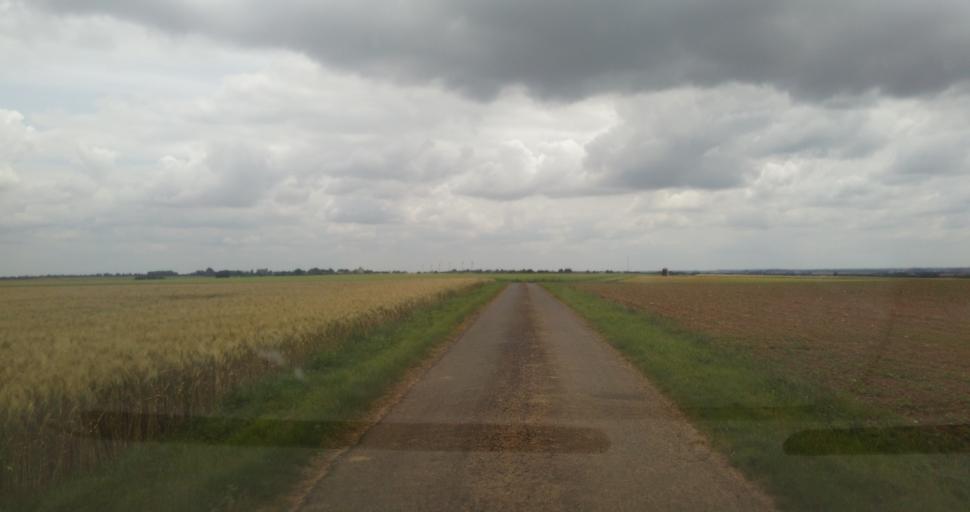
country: FR
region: Pays de la Loire
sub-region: Departement de la Vendee
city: Sainte-Gemme-la-Plaine
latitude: 46.5149
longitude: -1.0836
